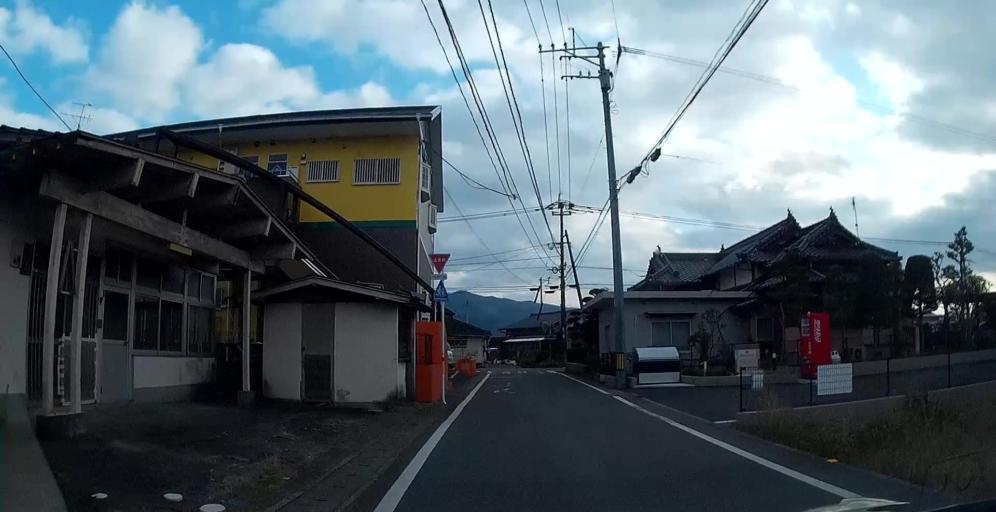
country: JP
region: Kumamoto
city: Yatsushiro
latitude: 32.5313
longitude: 130.6383
